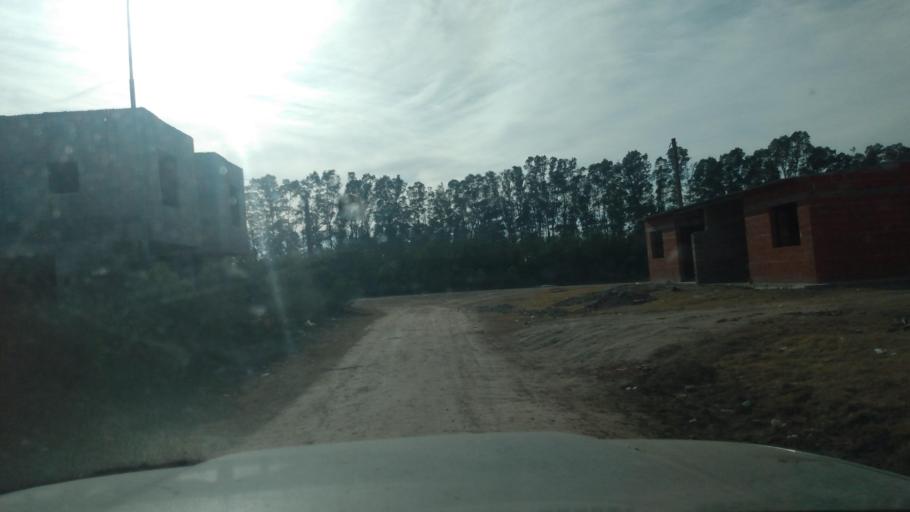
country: AR
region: Buenos Aires
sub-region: Partido de Lujan
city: Lujan
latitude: -34.5390
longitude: -59.1130
